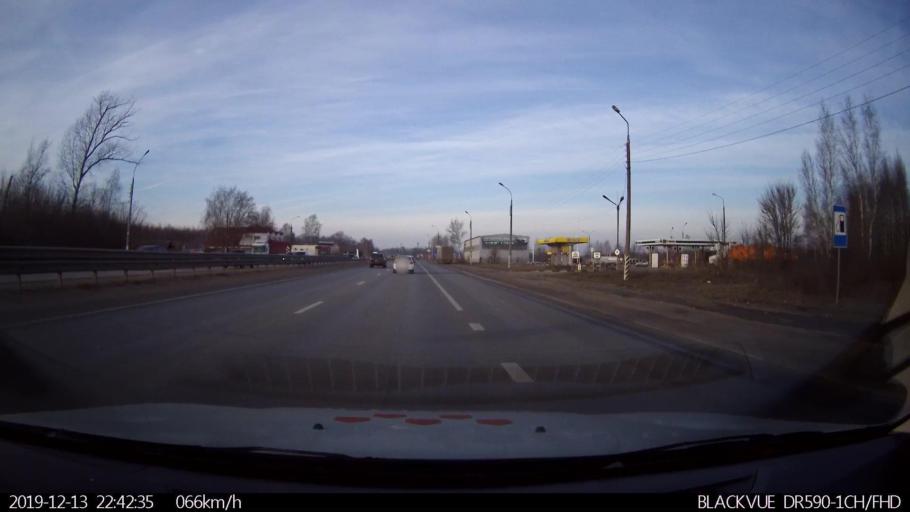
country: RU
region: Nizjnij Novgorod
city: Kstovo
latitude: 56.1906
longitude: 44.1335
